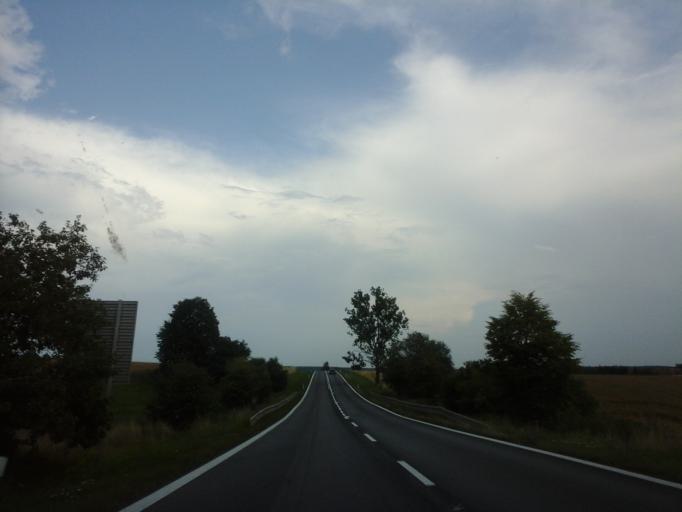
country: CZ
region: Pardubicky
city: Hradec nad Svitavou
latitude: 49.7074
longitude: 16.4888
